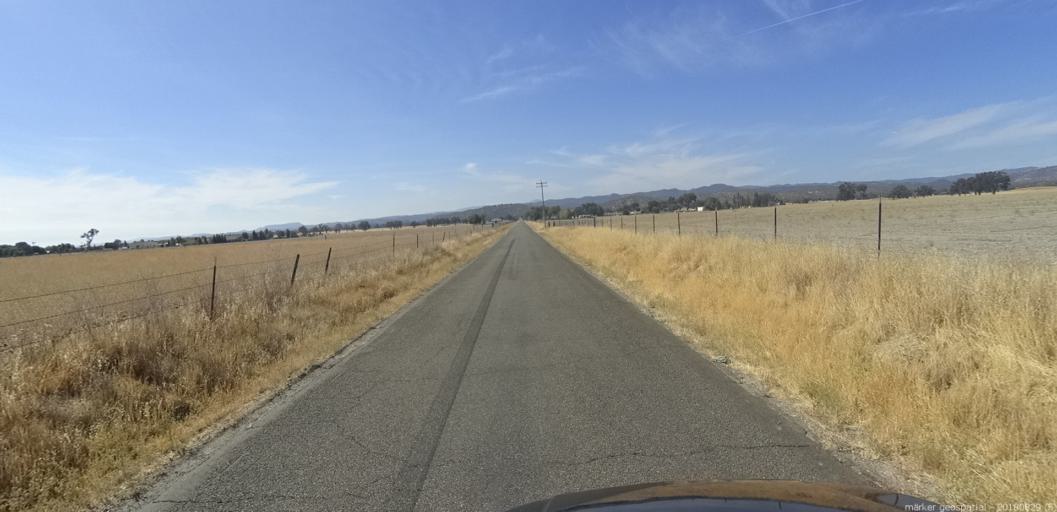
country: US
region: California
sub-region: Monterey County
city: King City
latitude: 35.9487
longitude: -121.0821
